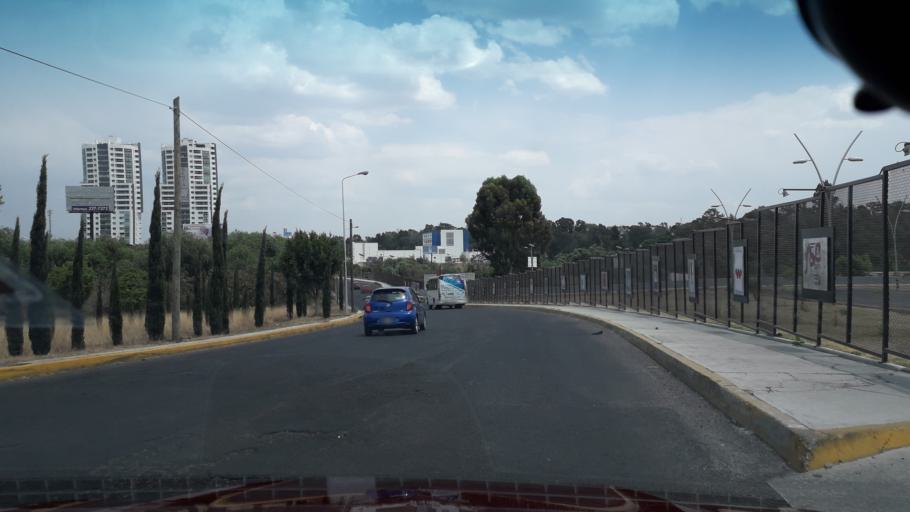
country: MX
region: Puebla
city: Puebla
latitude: 19.0204
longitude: -98.2383
